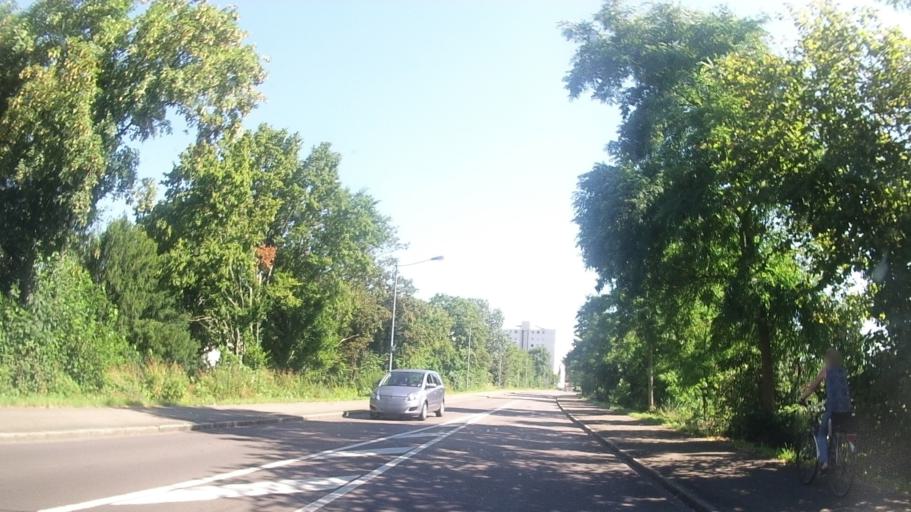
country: DE
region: Baden-Wuerttemberg
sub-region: Freiburg Region
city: Offenburg
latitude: 48.4843
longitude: 7.9388
